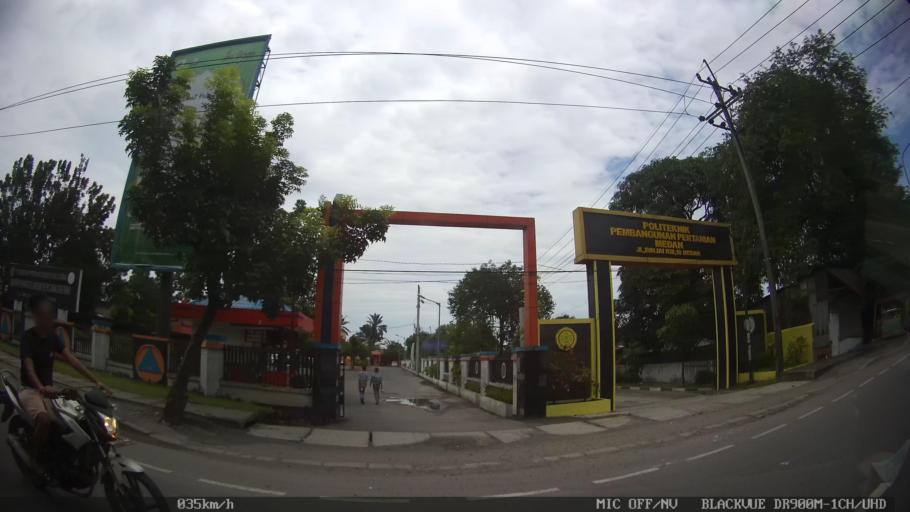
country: ID
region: North Sumatra
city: Sunggal
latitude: 3.5986
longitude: 98.5964
